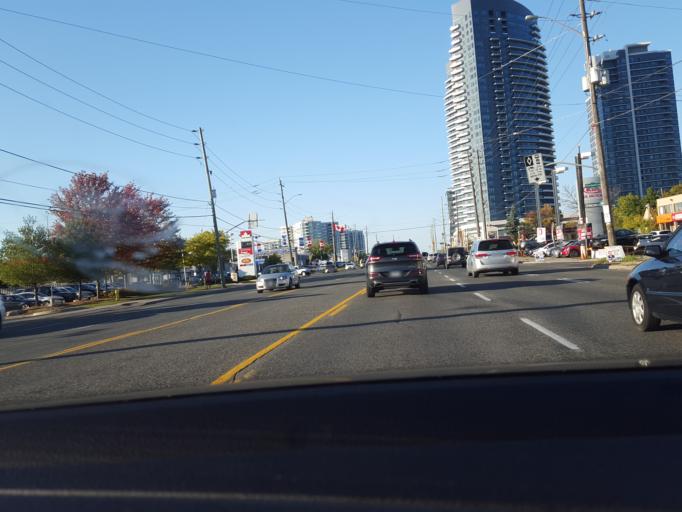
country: CA
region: Ontario
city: North York
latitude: 43.7995
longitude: -79.4204
